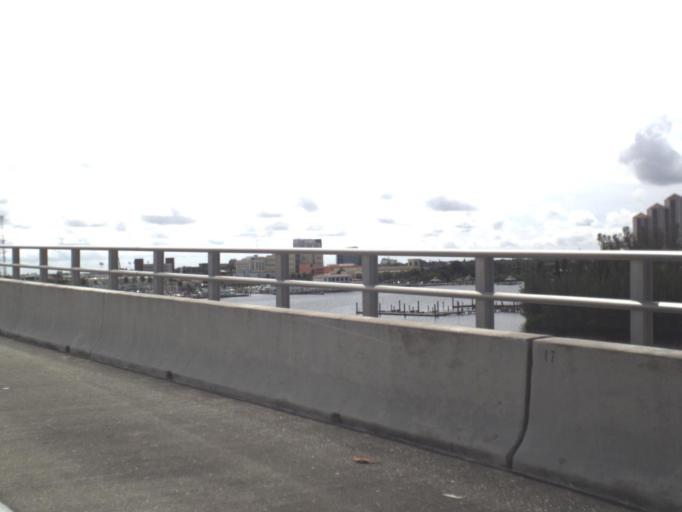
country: US
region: Florida
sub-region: Lee County
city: North Fort Myers
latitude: 26.6535
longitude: -81.8709
